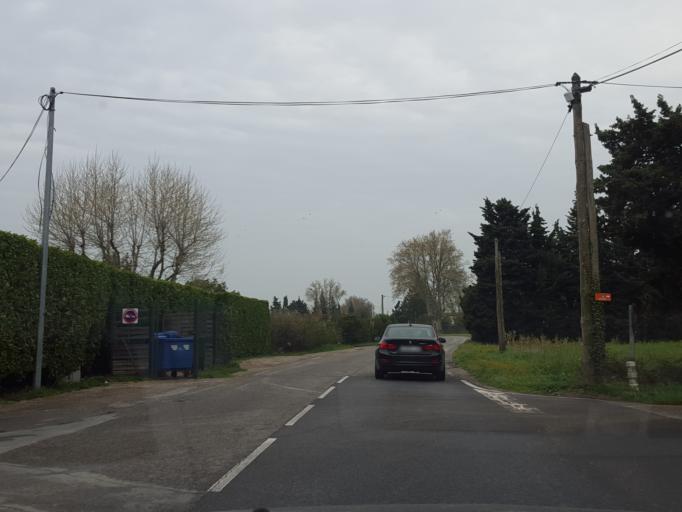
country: FR
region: Provence-Alpes-Cote d'Azur
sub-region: Departement du Vaucluse
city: Morieres-les-Avignon
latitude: 43.9241
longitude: 4.9011
